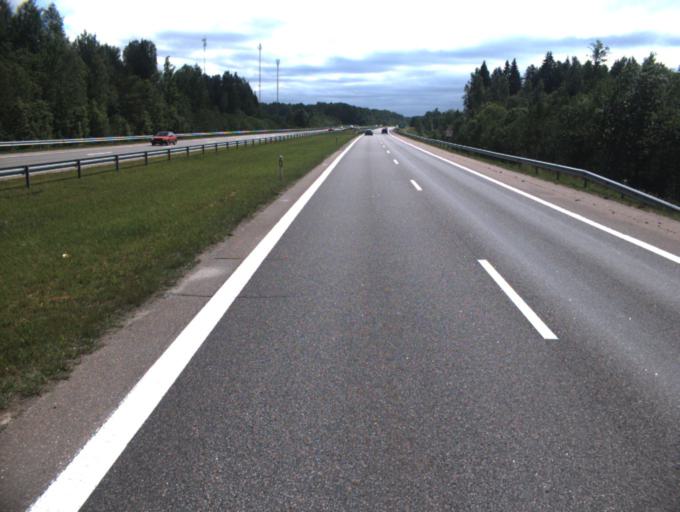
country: LT
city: Rietavas
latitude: 55.6451
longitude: 21.8597
